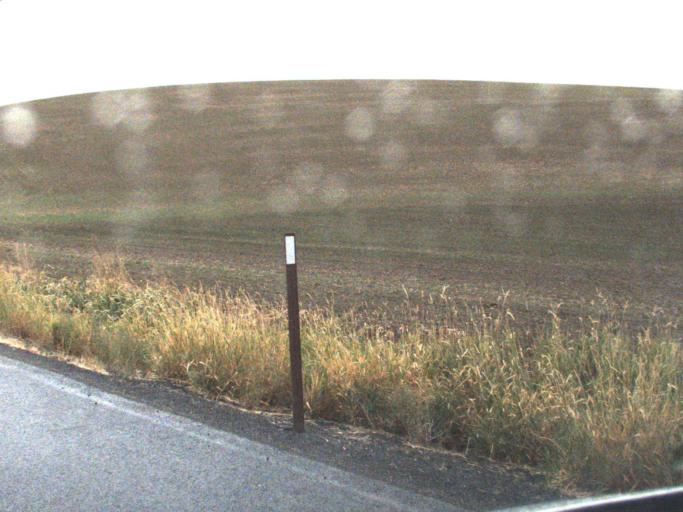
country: US
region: Washington
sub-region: Whitman County
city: Pullman
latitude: 46.7651
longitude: -117.2667
